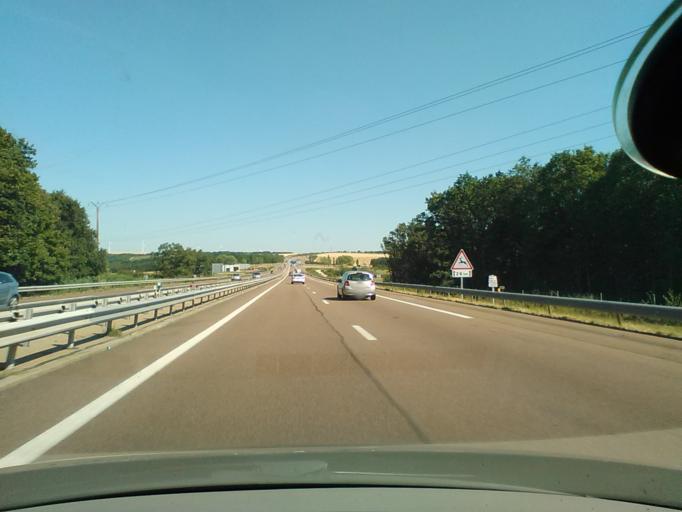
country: FR
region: Bourgogne
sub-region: Departement de l'Yonne
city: Venoy
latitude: 47.8022
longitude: 3.6393
